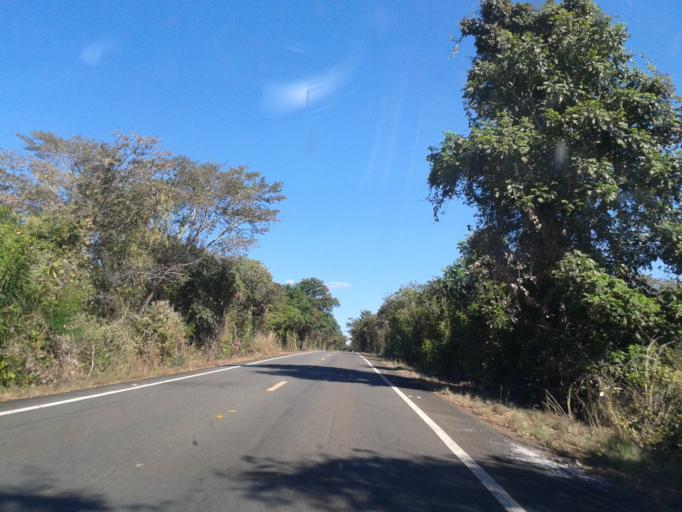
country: BR
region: Goias
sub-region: Sao Miguel Do Araguaia
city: Sao Miguel do Araguaia
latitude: -13.8047
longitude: -50.3423
